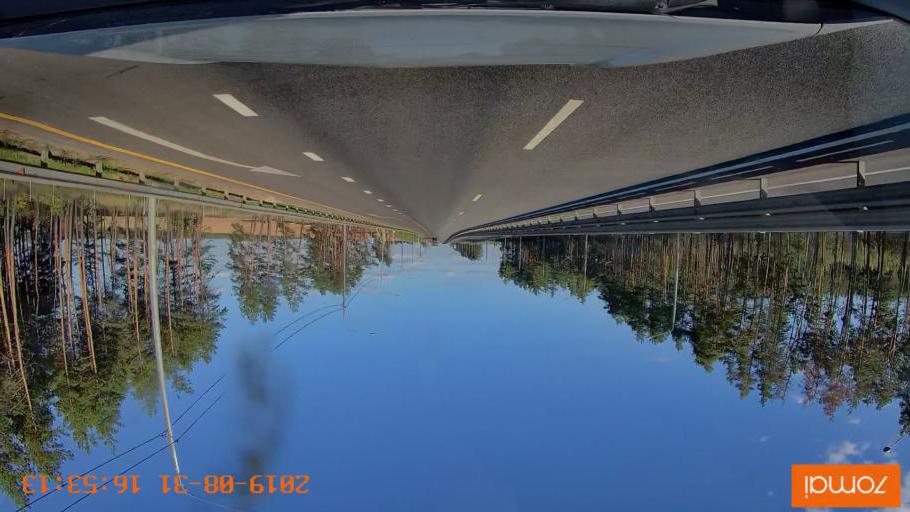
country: RU
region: Kaluga
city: Detchino
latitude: 54.7525
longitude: 36.2074
